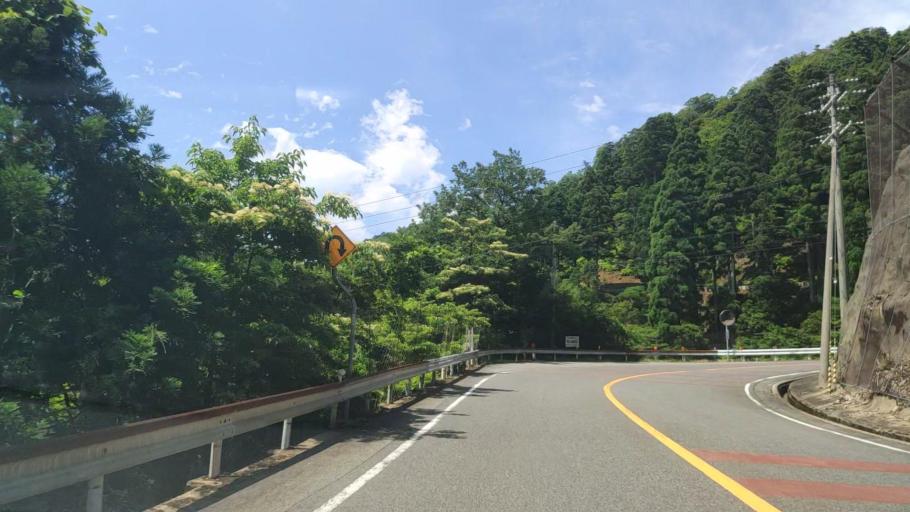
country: JP
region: Hyogo
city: Toyooka
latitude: 35.6363
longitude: 134.7805
